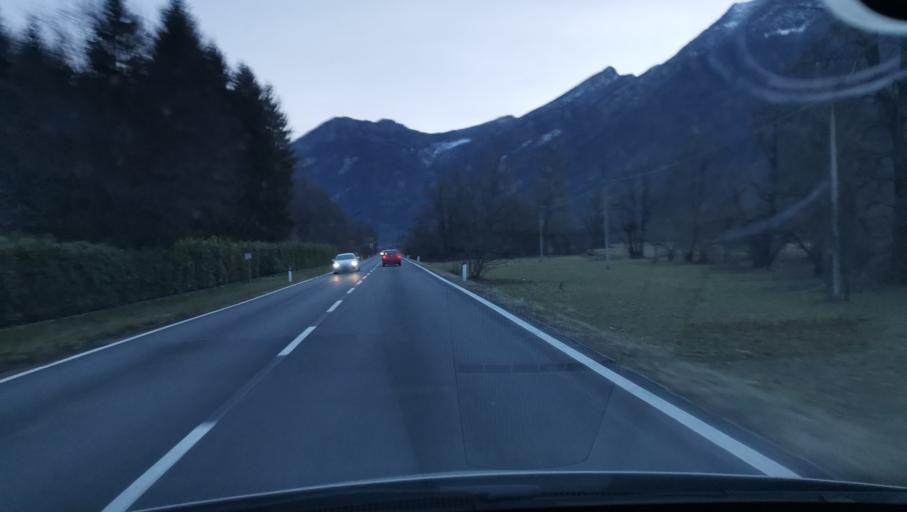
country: IT
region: Piedmont
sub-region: Provincia di Cuneo
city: Valloriate
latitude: 44.3120
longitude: 7.3510
